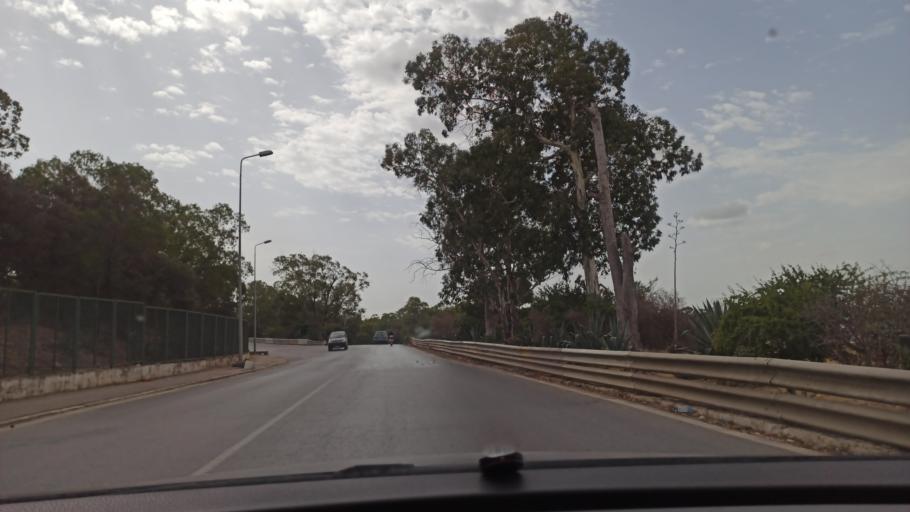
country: TN
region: Tunis
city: Tunis
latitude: 36.8275
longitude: 10.1672
